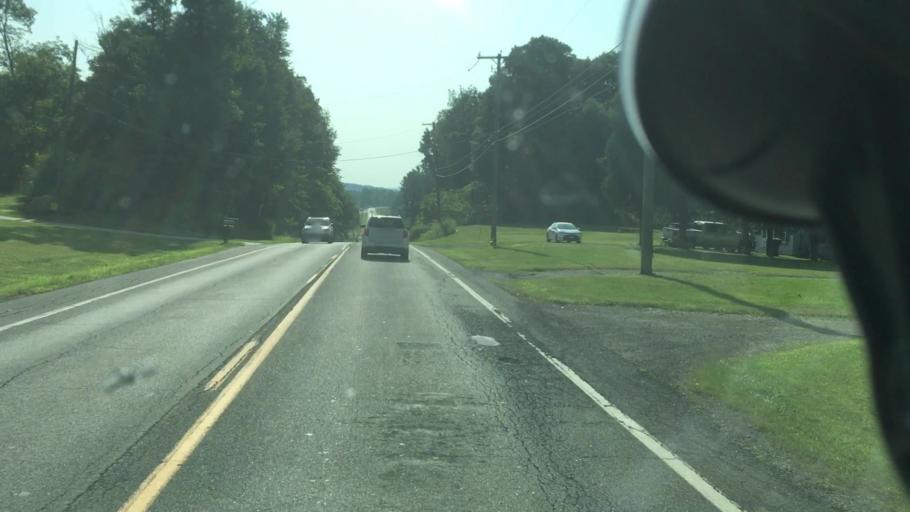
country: US
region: Ohio
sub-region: Mahoning County
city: Lowellville
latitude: 41.0239
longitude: -80.5329
